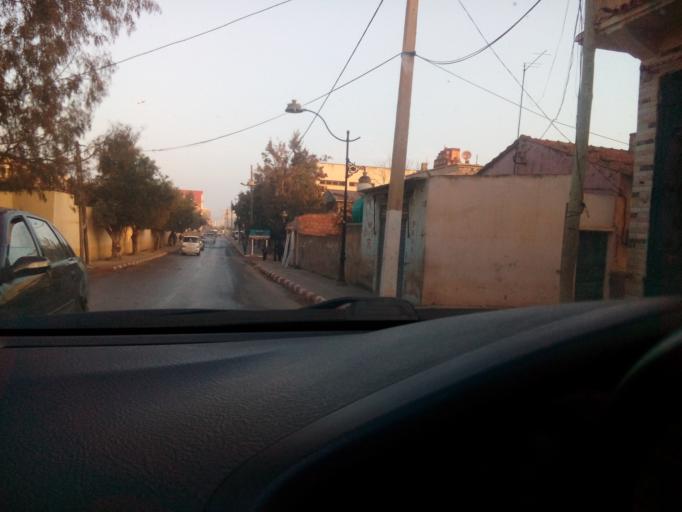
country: DZ
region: Oran
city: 'Ain el Turk
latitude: 35.7401
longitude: -0.7727
